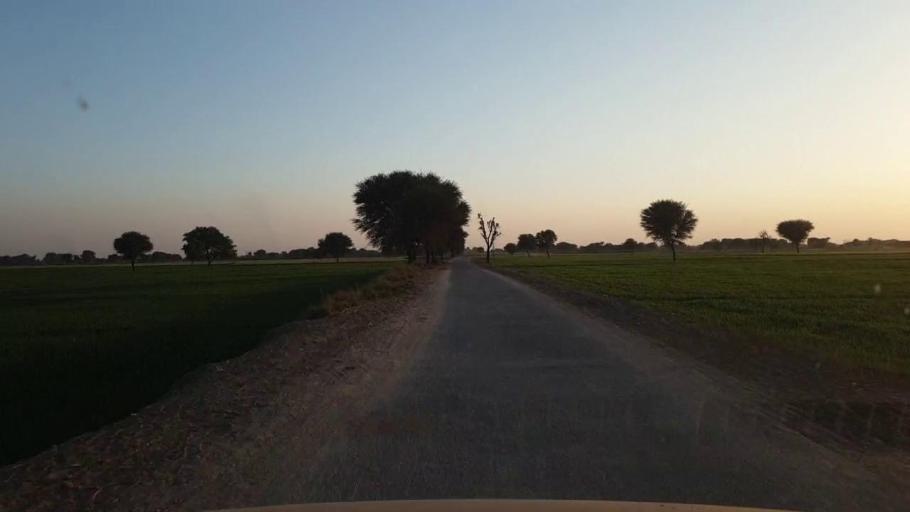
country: PK
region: Sindh
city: Tando Jam
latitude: 25.3090
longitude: 68.6394
